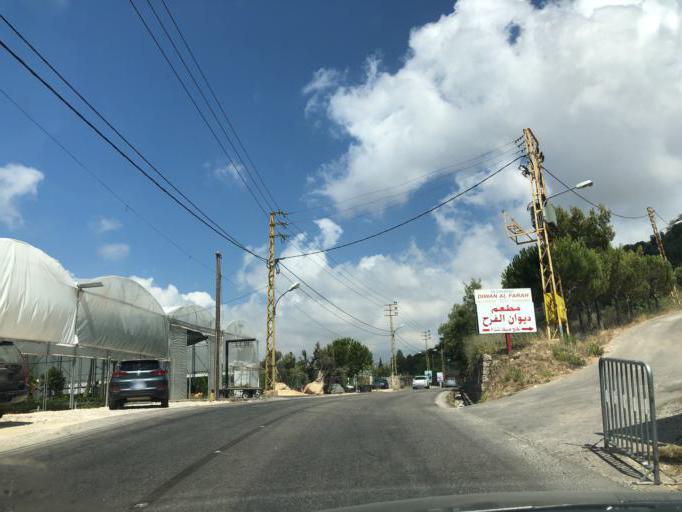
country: LB
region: Mont-Liban
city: Beit ed Dine
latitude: 33.6979
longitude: 35.5908
